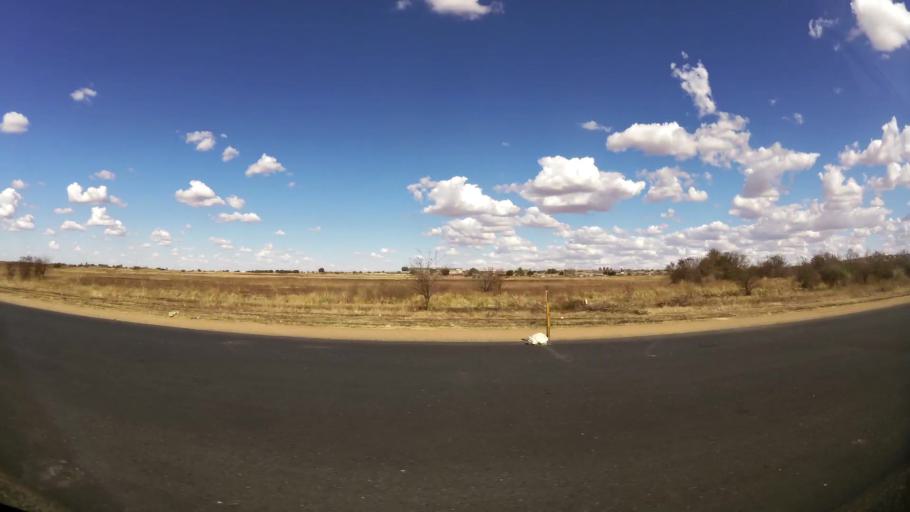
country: ZA
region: North-West
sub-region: Dr Kenneth Kaunda District Municipality
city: Klerksdorp
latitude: -26.8731
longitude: 26.6054
